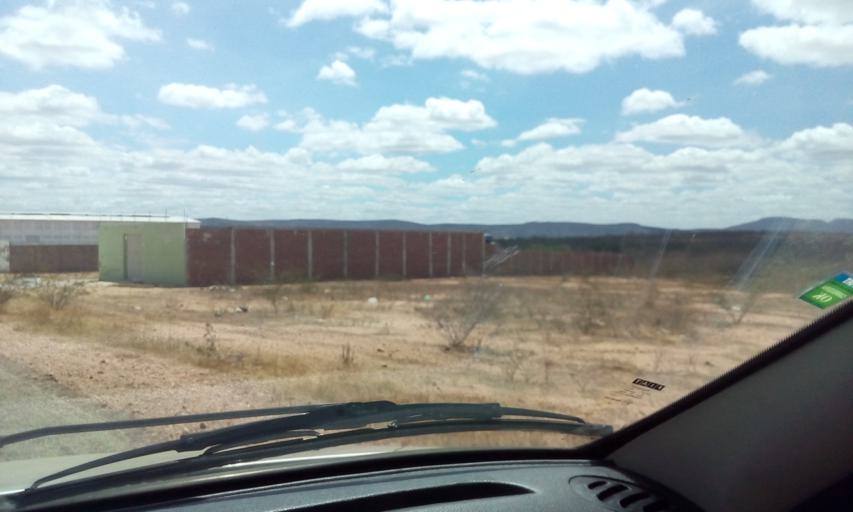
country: BR
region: Rio Grande do Norte
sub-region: Currais Novos
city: Currais Novos
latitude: -6.2779
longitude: -36.5351
